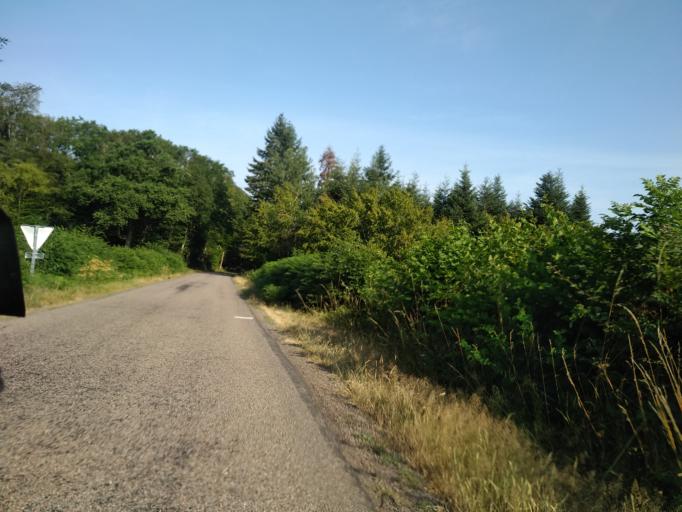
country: FR
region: Rhone-Alpes
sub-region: Departement de la Loire
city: Saint-Nizier-sous-Charlieu
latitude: 46.2405
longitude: 4.1254
